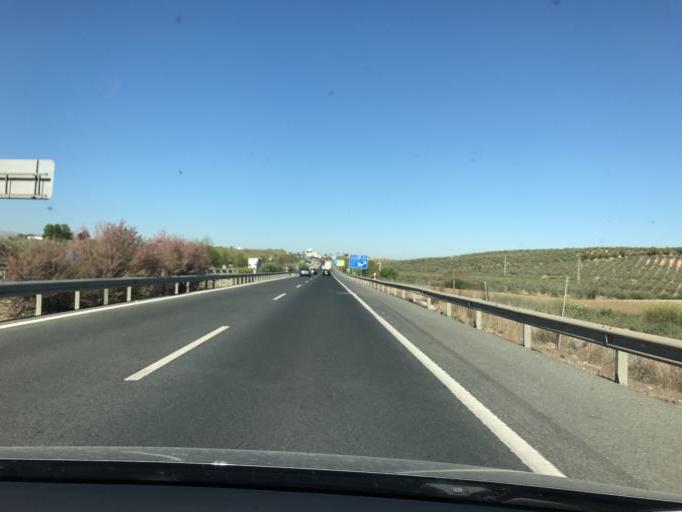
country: ES
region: Andalusia
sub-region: Provincia de Granada
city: Moraleda de Zafayona
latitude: 37.1797
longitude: -3.9158
